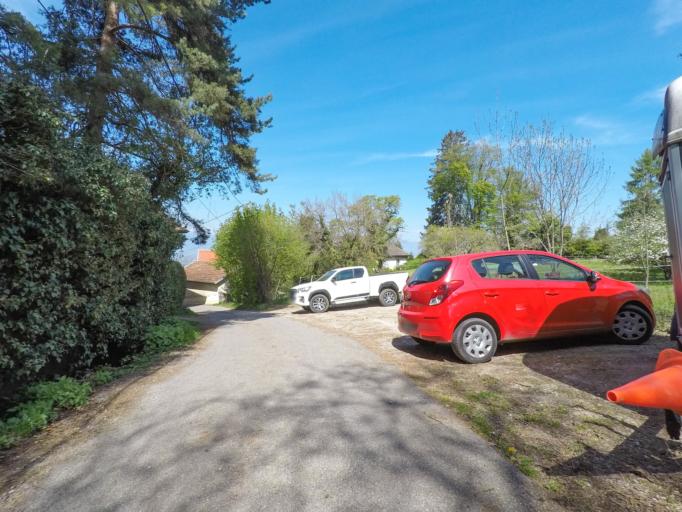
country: FR
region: Rhone-Alpes
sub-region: Departement de la Haute-Savoie
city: Collonges-sous-Saleve
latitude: 46.1276
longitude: 6.1526
